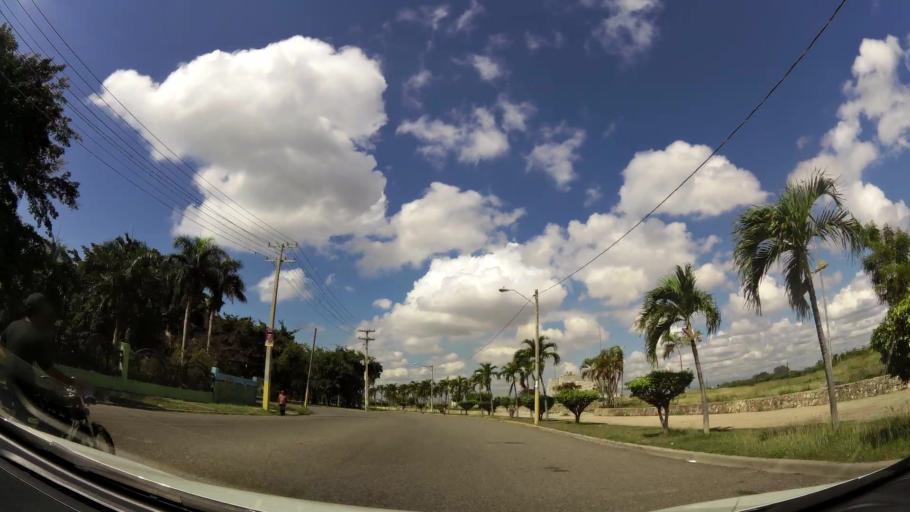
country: DO
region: Santo Domingo
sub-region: Santo Domingo
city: Santo Domingo Este
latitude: 18.4786
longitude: -69.8637
